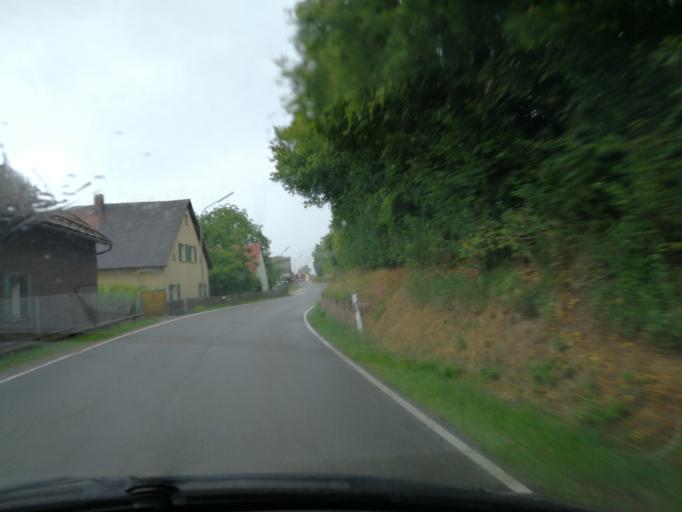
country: DE
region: Bavaria
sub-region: Upper Palatinate
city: Donaustauf
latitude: 49.0236
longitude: 12.2651
